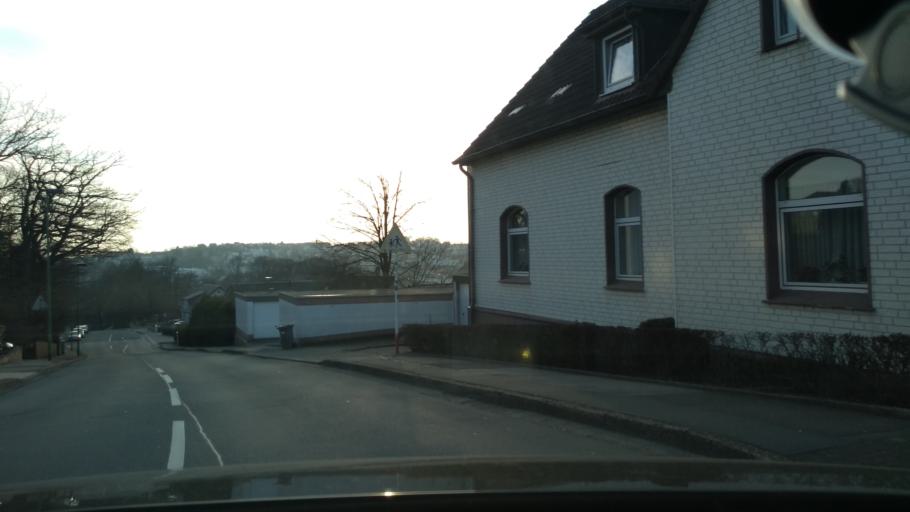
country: DE
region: North Rhine-Westphalia
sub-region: Regierungsbezirk Arnsberg
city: Luedenscheid
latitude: 51.2183
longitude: 7.6601
